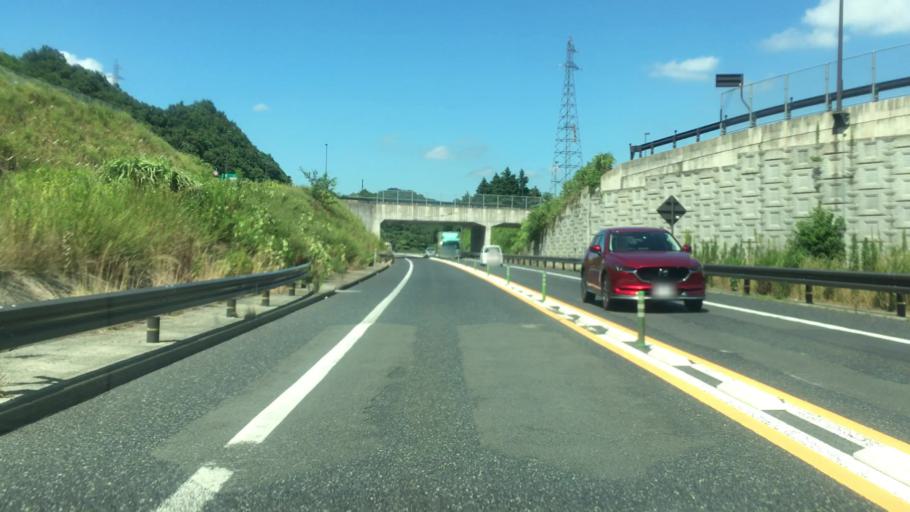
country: JP
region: Tottori
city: Tottori
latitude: 35.3550
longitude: 134.1958
